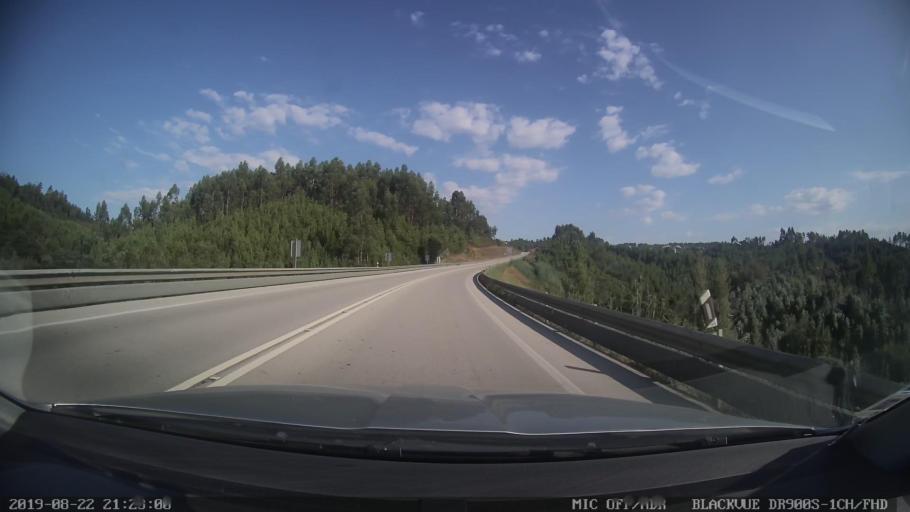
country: PT
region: Castelo Branco
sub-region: Serta
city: Serta
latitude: 39.8248
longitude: -8.1062
